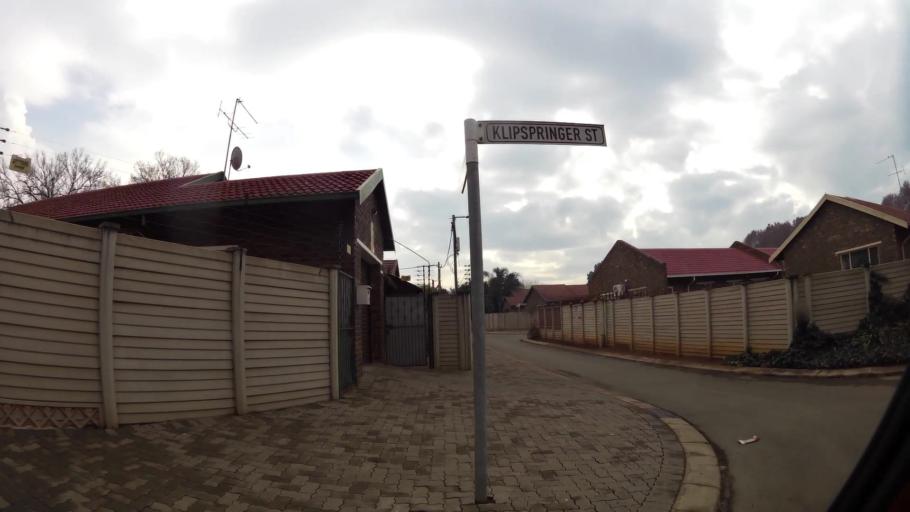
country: ZA
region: Gauteng
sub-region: Sedibeng District Municipality
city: Vanderbijlpark
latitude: -26.7025
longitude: 27.8423
